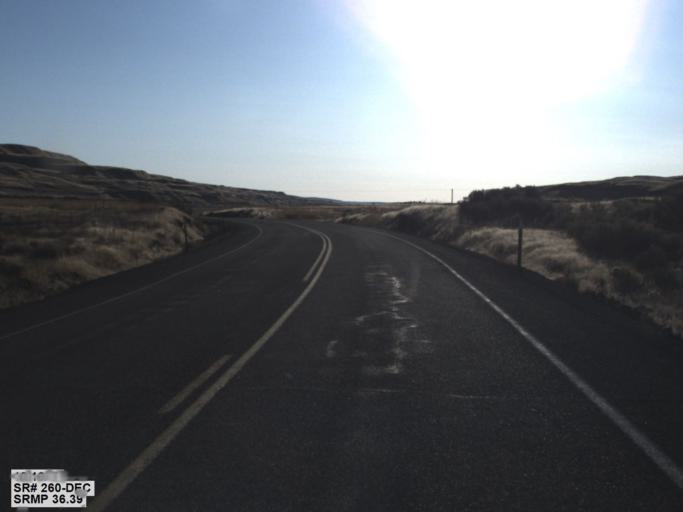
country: US
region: Washington
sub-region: Adams County
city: Ritzville
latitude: 46.7306
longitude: -118.3565
